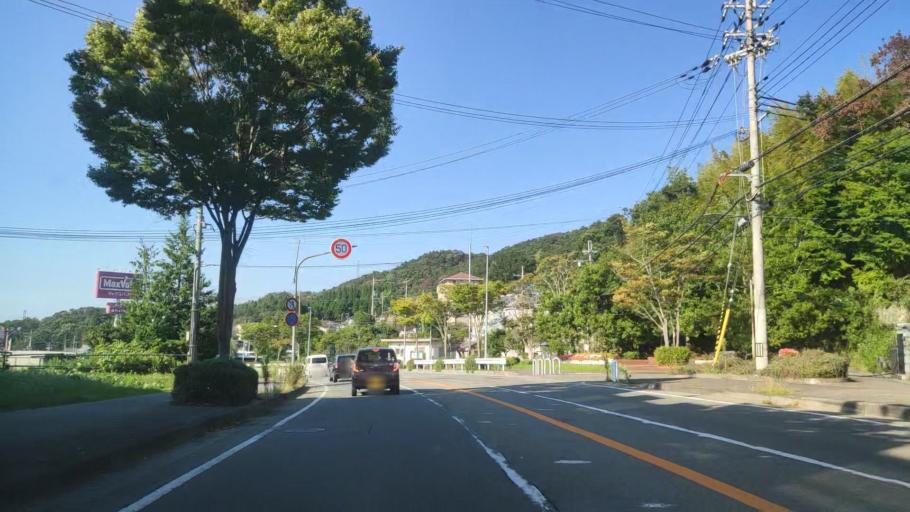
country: JP
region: Hyogo
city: Kobe
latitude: 34.7807
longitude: 135.1967
